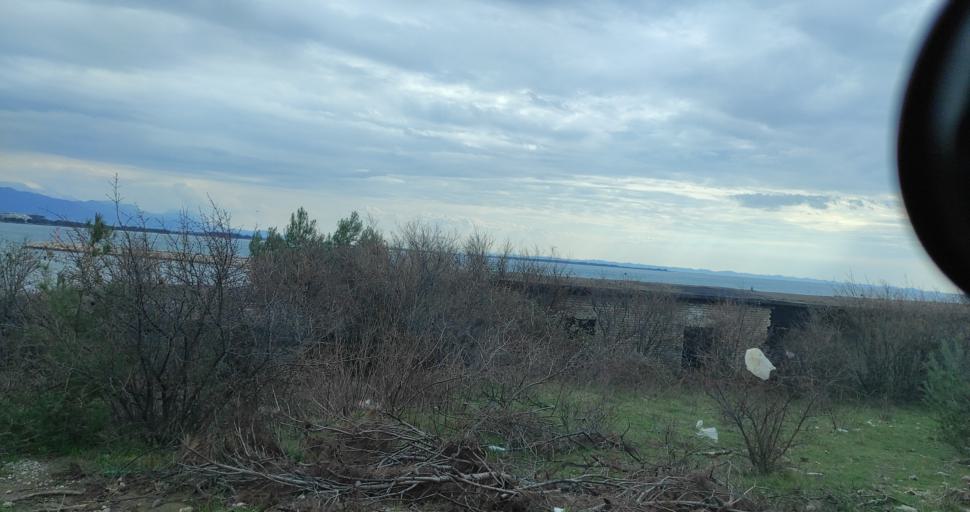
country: AL
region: Lezhe
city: Shengjin
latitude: 41.8101
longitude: 19.5841
